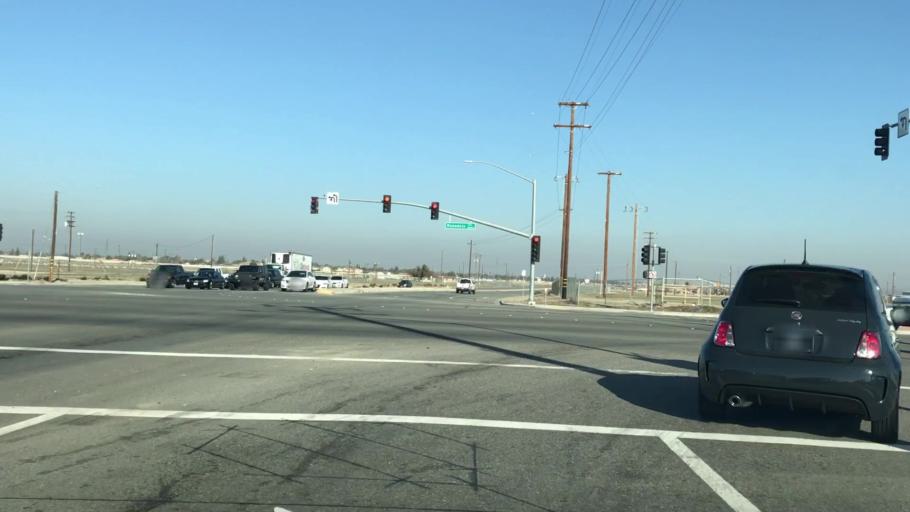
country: US
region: California
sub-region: Kern County
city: Greenacres
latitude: 35.3830
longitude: -119.0654
